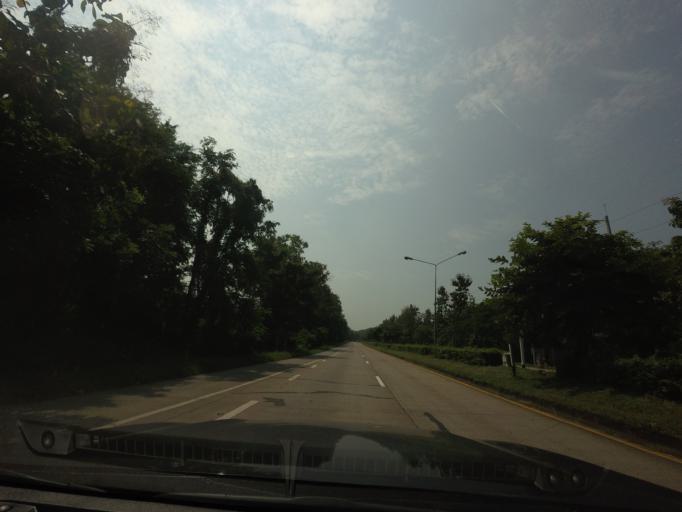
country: TH
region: Phrae
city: Sung Men
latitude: 18.0029
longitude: 100.1038
